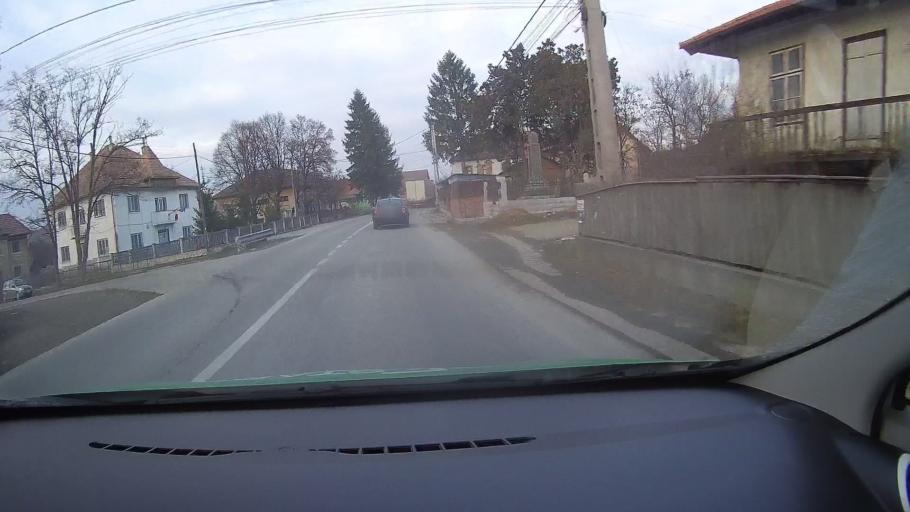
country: RO
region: Harghita
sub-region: Comuna Simonesti
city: Simonesti
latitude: 46.3354
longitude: 25.1073
